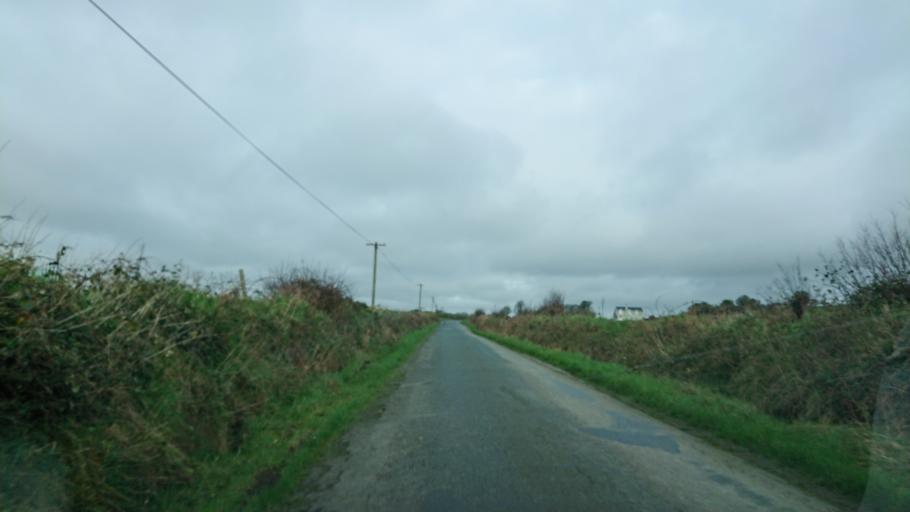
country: IE
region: Munster
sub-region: Waterford
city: Portlaw
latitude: 52.1730
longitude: -7.3053
